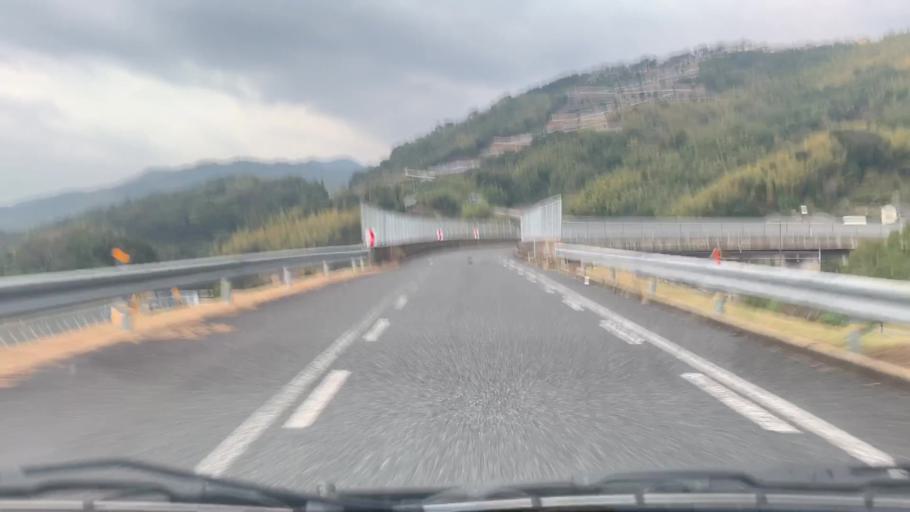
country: JP
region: Nagasaki
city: Nagasaki-shi
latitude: 32.7281
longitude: 129.9050
